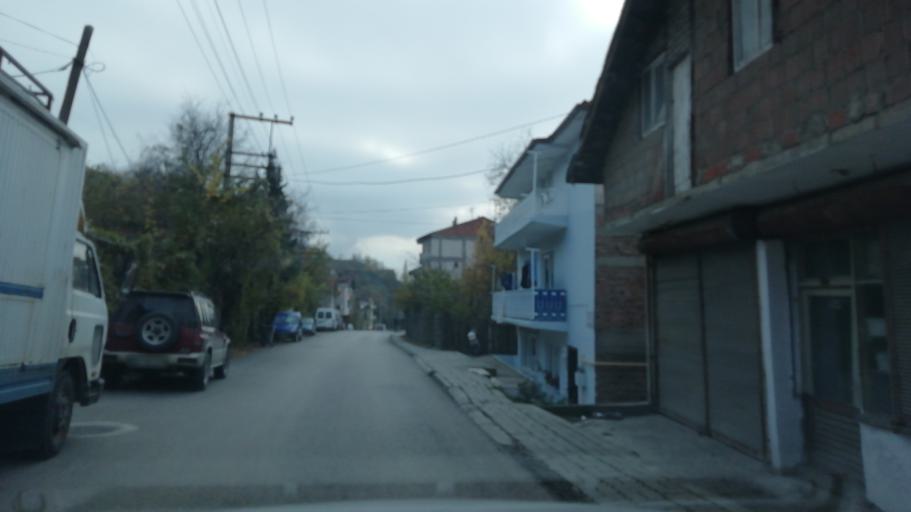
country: TR
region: Karabuk
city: Karabuk
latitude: 41.2134
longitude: 32.6286
